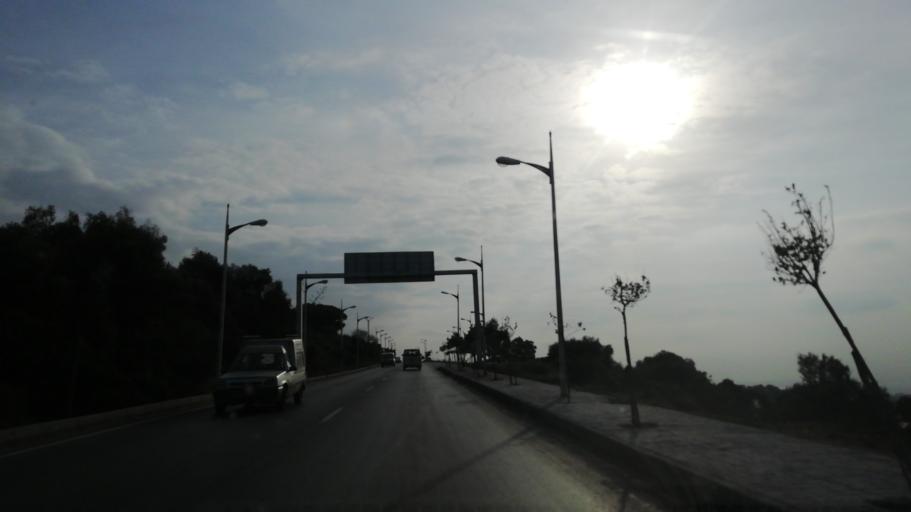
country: DZ
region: Mostaganem
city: Mostaganem
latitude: 35.9093
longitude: 0.0786
